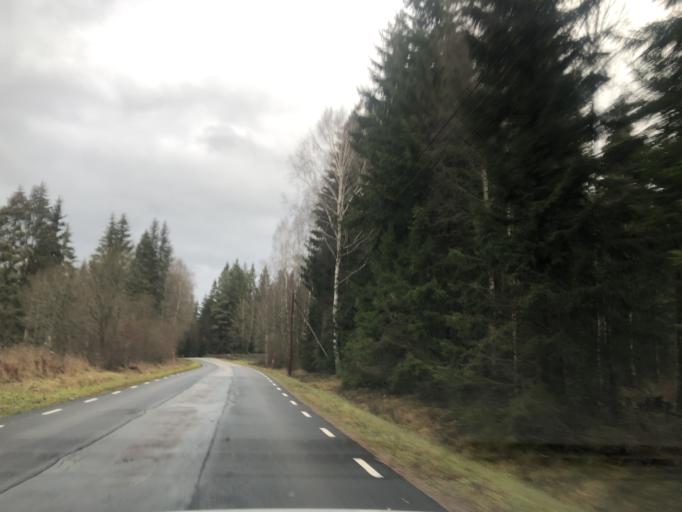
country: SE
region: Vaestra Goetaland
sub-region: Boras Kommun
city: Dalsjofors
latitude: 57.8119
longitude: 13.1990
